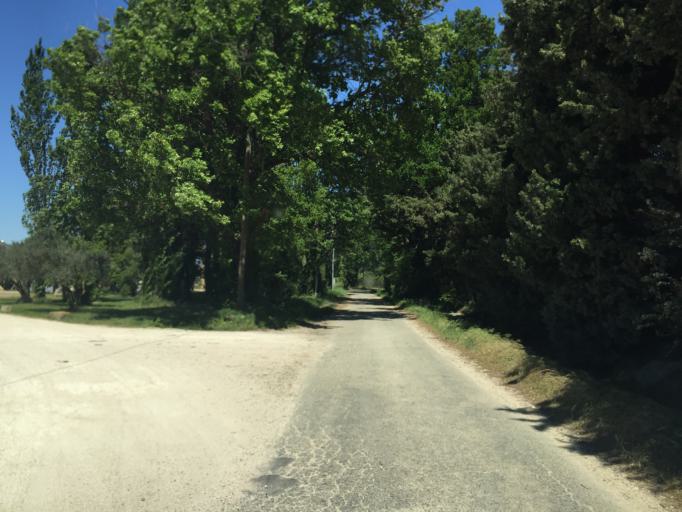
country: FR
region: Provence-Alpes-Cote d'Azur
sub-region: Departement du Vaucluse
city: Jonquieres
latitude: 44.1320
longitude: 4.9100
